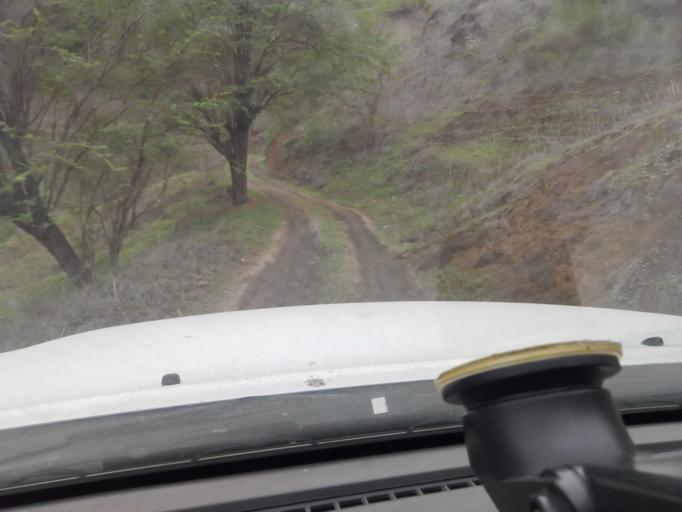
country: CV
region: Sao Salvador do Mundo
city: Picos
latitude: 15.1418
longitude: -23.6333
